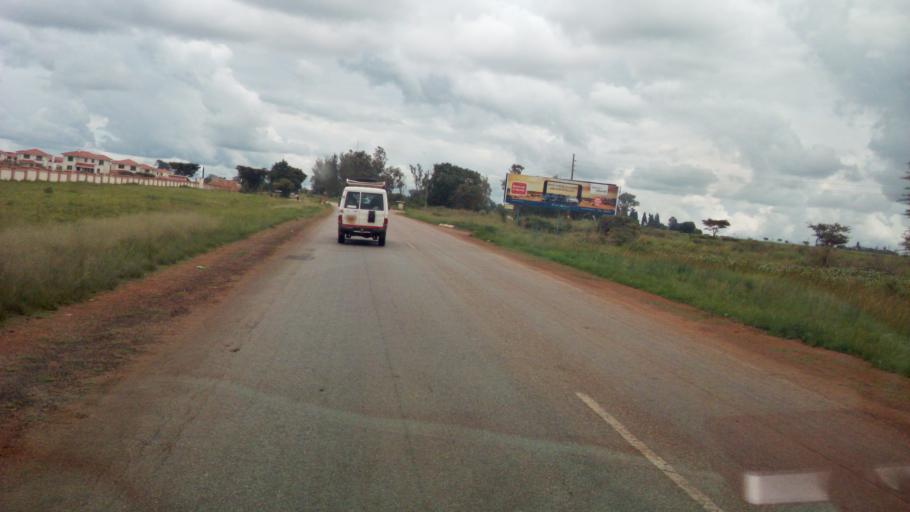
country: ZW
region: Harare
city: Harare
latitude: -17.7380
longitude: 31.0251
